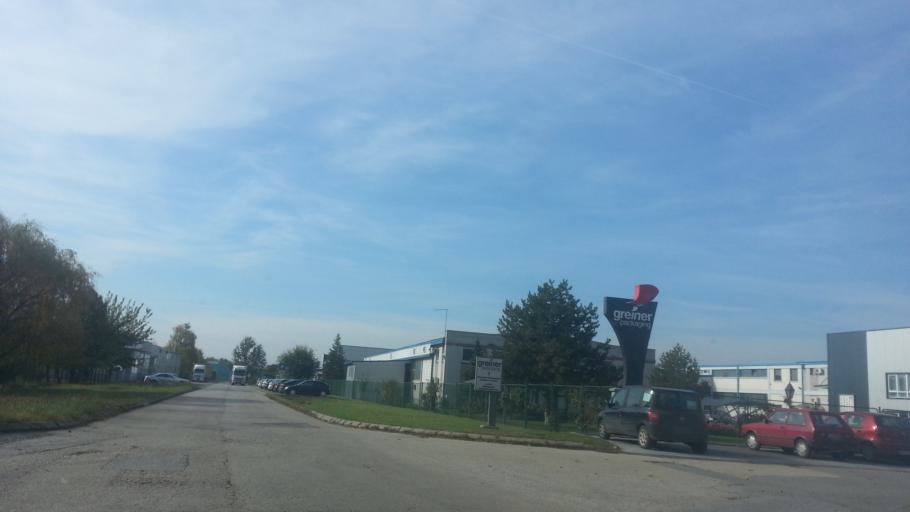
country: RS
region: Autonomna Pokrajina Vojvodina
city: Nova Pazova
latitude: 44.9522
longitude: 20.2059
